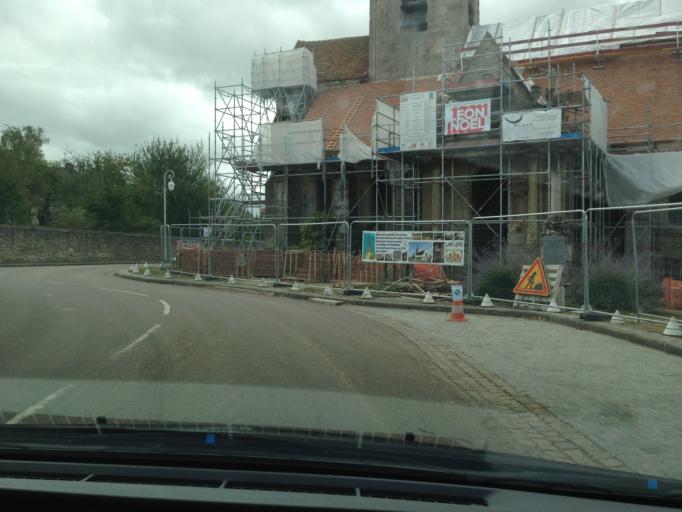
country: FR
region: Ile-de-France
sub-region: Departement du Val-d'Oise
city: Ennery
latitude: 49.0953
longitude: 2.0952
